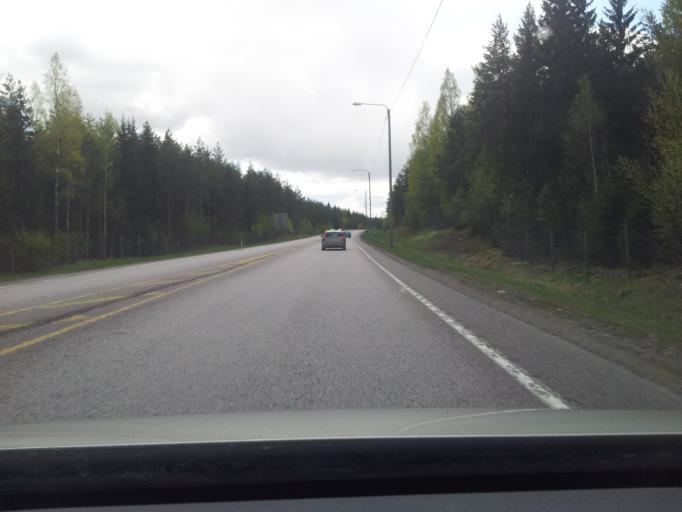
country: FI
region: Uusimaa
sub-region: Loviisa
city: Perna
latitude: 60.5128
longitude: 25.9649
